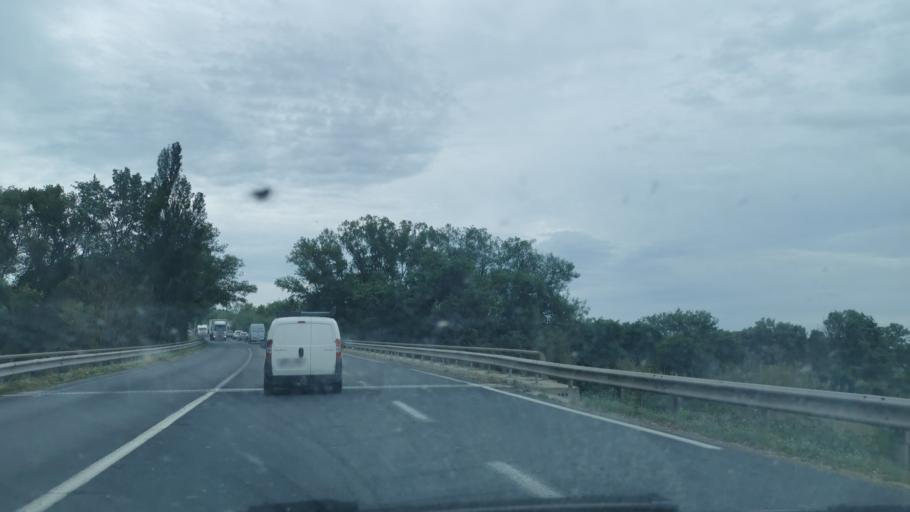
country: FR
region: Languedoc-Roussillon
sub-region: Departement de l'Herault
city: Balaruc-le-Vieux
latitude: 43.4708
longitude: 3.6881
